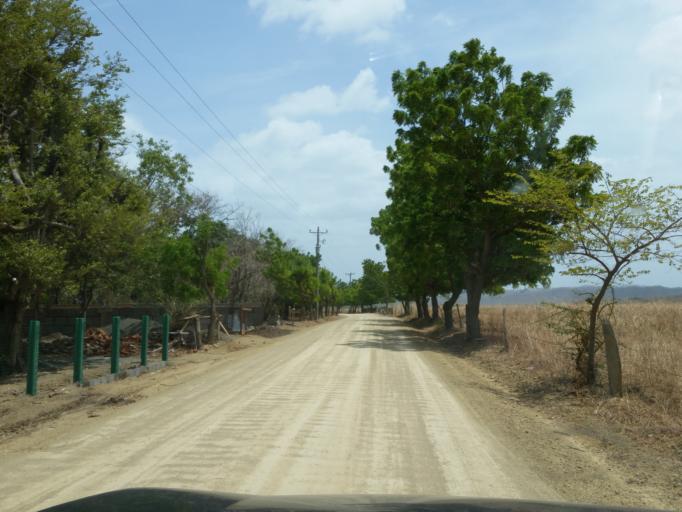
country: NI
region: Rivas
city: Tola
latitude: 11.4279
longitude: -86.0235
